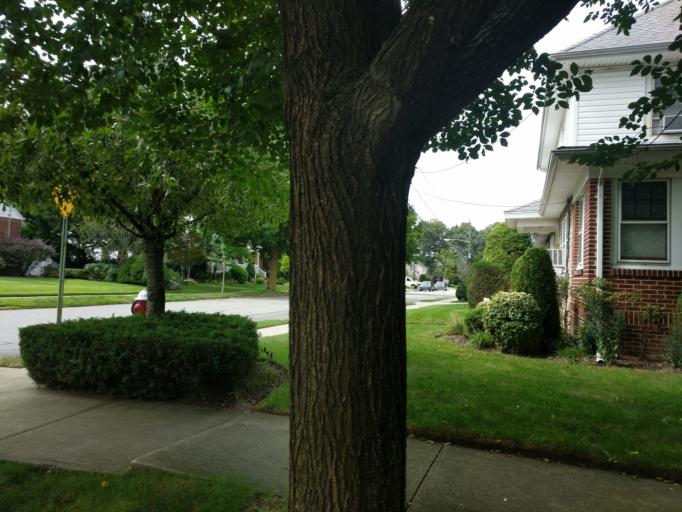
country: US
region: New York
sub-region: Nassau County
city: Malverne
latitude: 40.6731
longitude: -73.6812
